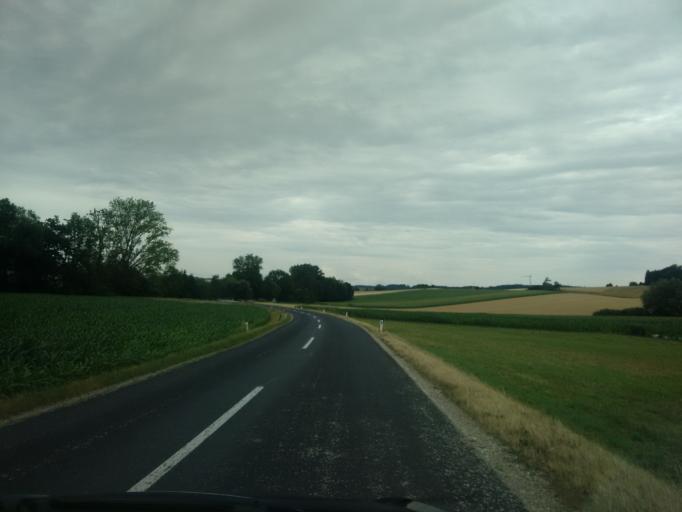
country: AT
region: Upper Austria
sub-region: Politischer Bezirk Grieskirchen
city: Bad Schallerbach
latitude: 48.1974
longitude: 13.8879
